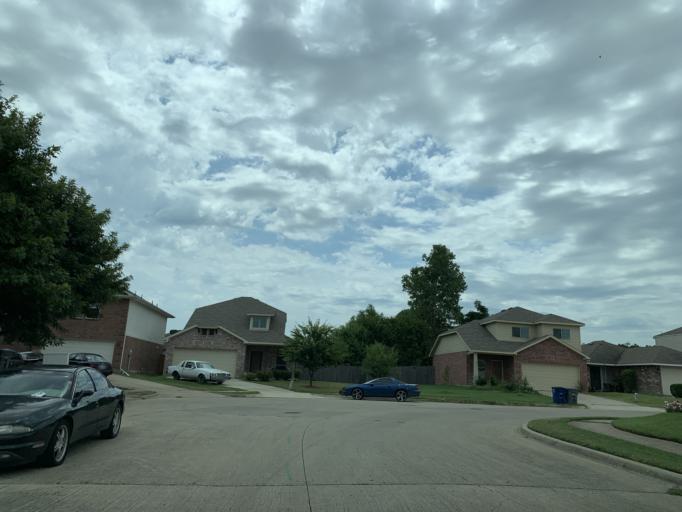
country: US
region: Texas
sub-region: Dallas County
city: DeSoto
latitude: 32.6549
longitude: -96.8190
